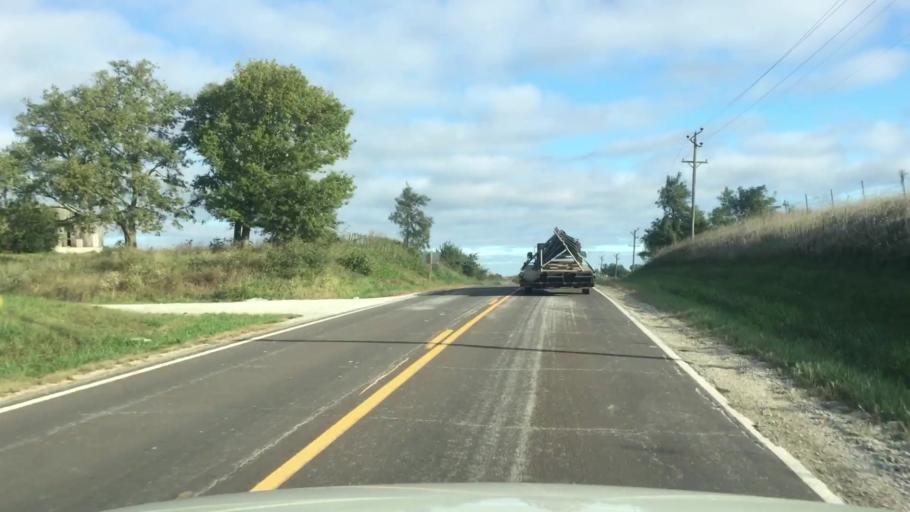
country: US
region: Missouri
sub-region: Howard County
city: New Franklin
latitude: 39.0749
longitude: -92.7457
